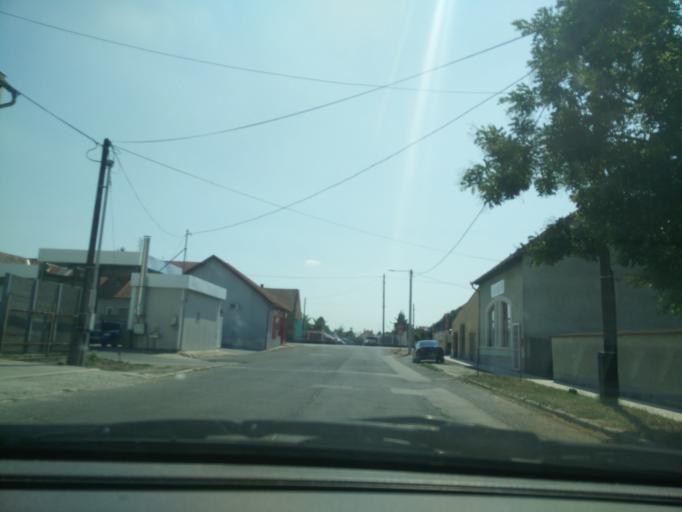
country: HU
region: Heves
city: Hatvan
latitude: 47.6669
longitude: 19.6973
